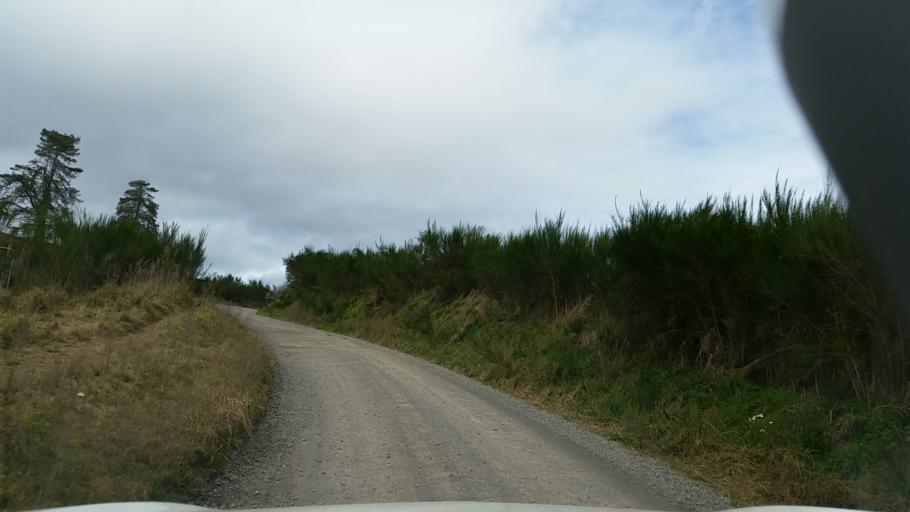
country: NZ
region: Bay of Plenty
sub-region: Whakatane District
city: Murupara
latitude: -38.3403
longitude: 176.5398
